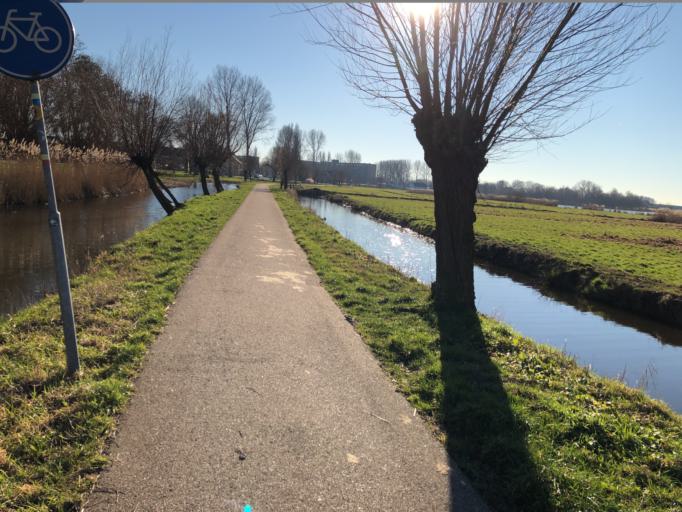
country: NL
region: North Holland
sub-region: Gemeente Uitgeest
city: Uitgeest
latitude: 52.5102
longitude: 4.7553
